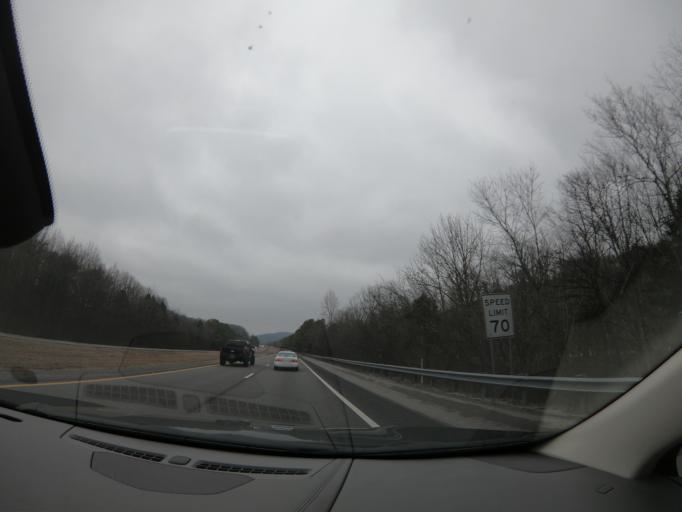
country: US
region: Tennessee
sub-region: Rutherford County
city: Plainview
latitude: 35.6304
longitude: -86.2452
